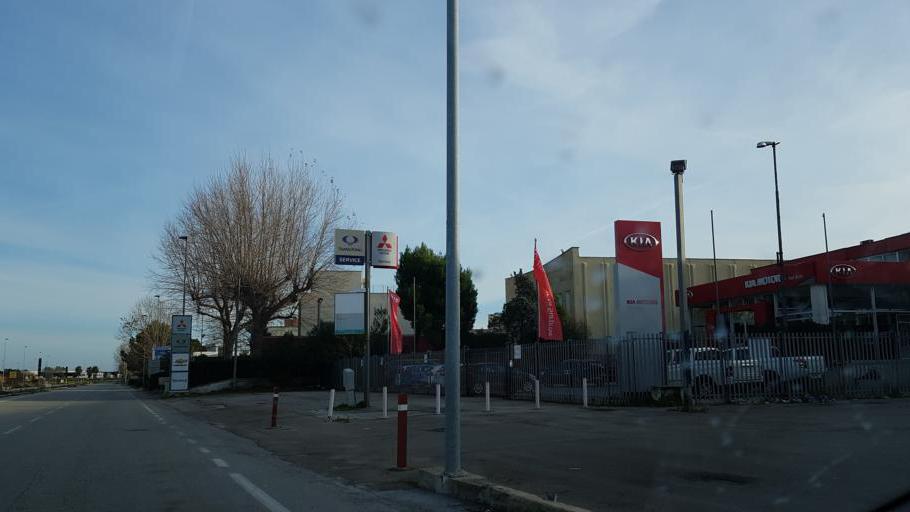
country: IT
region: Apulia
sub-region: Provincia di Brindisi
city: Brindisi
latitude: 40.6309
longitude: 17.9573
